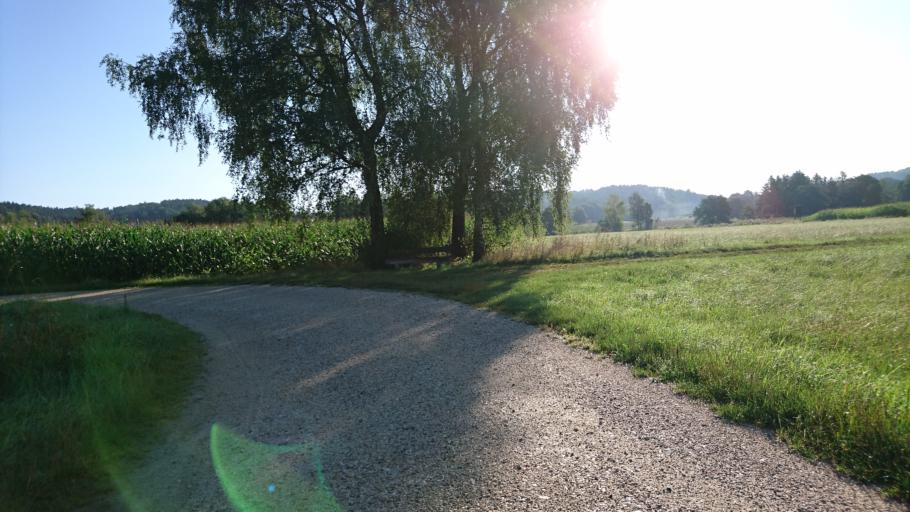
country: DE
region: Bavaria
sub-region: Swabia
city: Altenmunster
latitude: 48.4474
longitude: 10.5927
